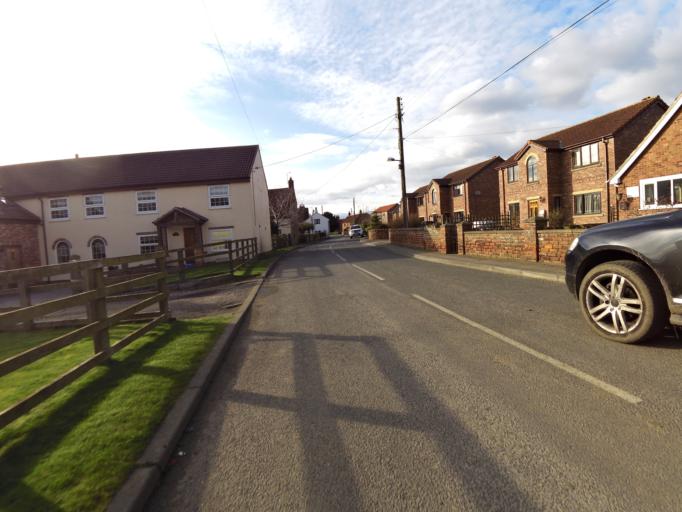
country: GB
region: England
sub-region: East Riding of Yorkshire
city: Pollington
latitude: 53.7127
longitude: -1.0732
